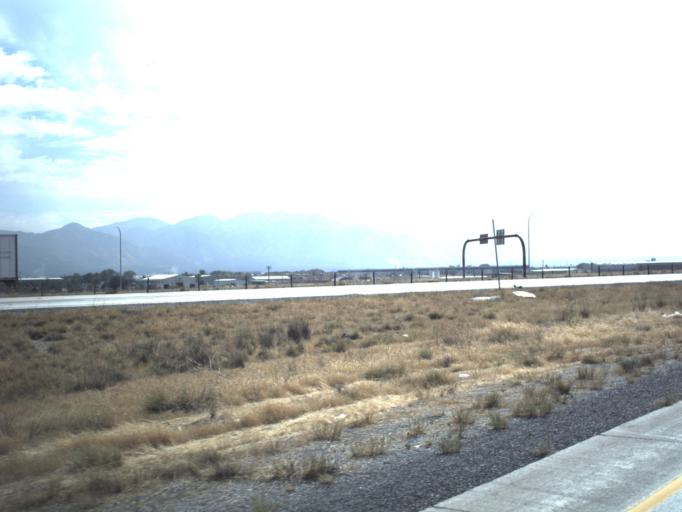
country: US
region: Utah
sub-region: Salt Lake County
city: West Valley City
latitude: 40.7614
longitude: -111.9875
